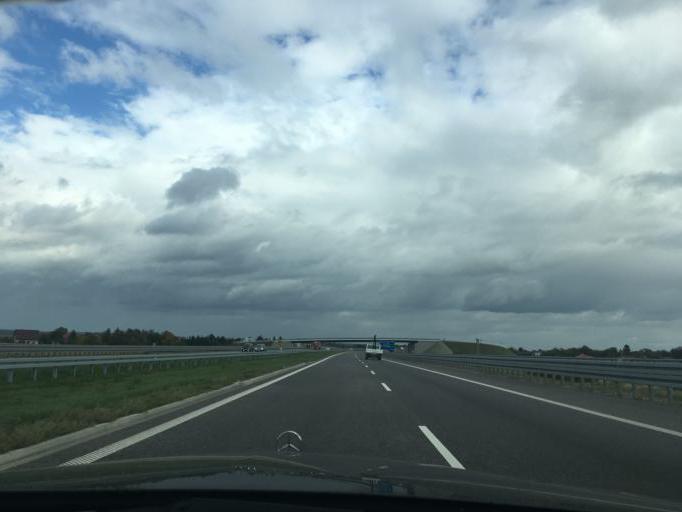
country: PL
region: Subcarpathian Voivodeship
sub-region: Powiat lancucki
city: Czarna
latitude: 50.0952
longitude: 22.2061
